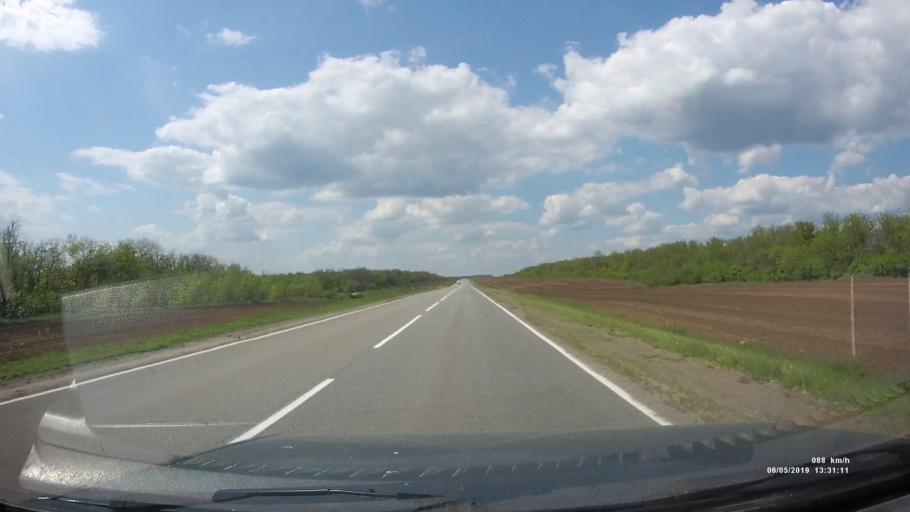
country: RU
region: Rostov
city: Ust'-Donetskiy
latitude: 47.6749
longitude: 40.8142
